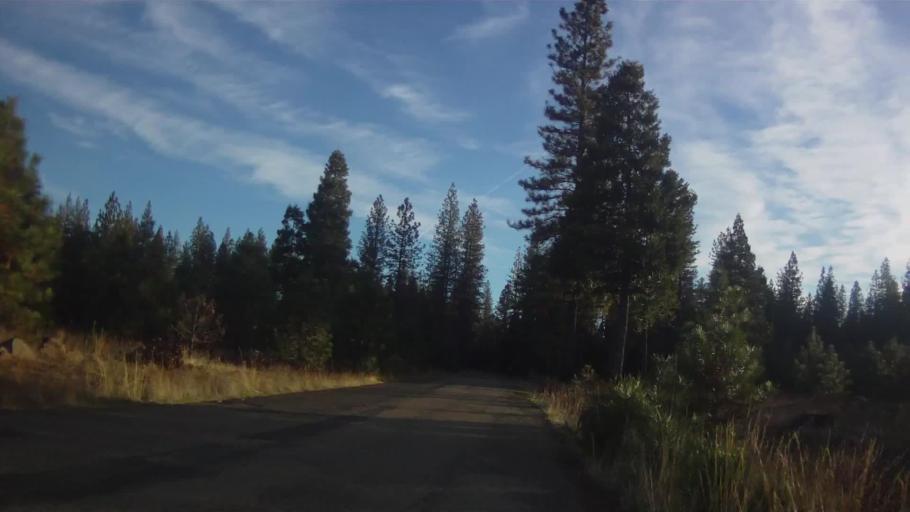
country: US
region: California
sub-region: Shasta County
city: Shingletown
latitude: 40.6256
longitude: -121.8571
